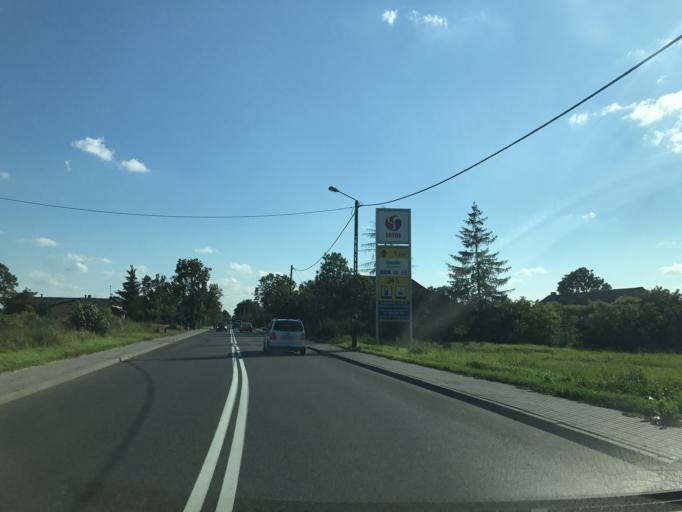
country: PL
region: Kujawsko-Pomorskie
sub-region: Powiat wloclawski
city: Brzesc Kujawski
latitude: 52.6225
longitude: 18.9540
